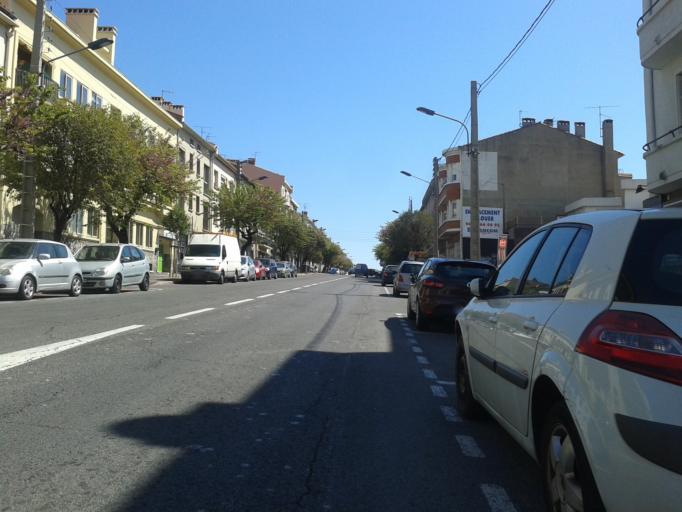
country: FR
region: Languedoc-Roussillon
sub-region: Departement des Pyrenees-Orientales
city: Perpignan
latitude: 42.6914
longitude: 2.8949
